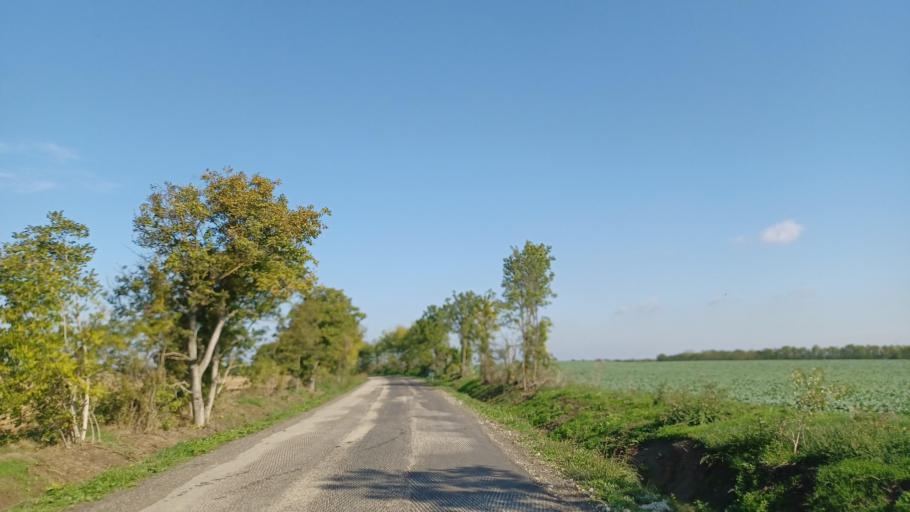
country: HU
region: Tolna
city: Nagydorog
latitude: 46.5821
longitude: 18.5956
